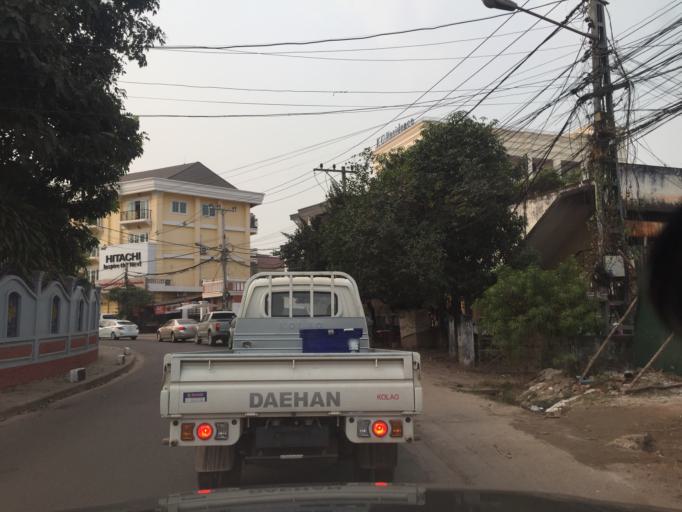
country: LA
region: Vientiane
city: Vientiane
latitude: 17.9723
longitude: 102.6162
